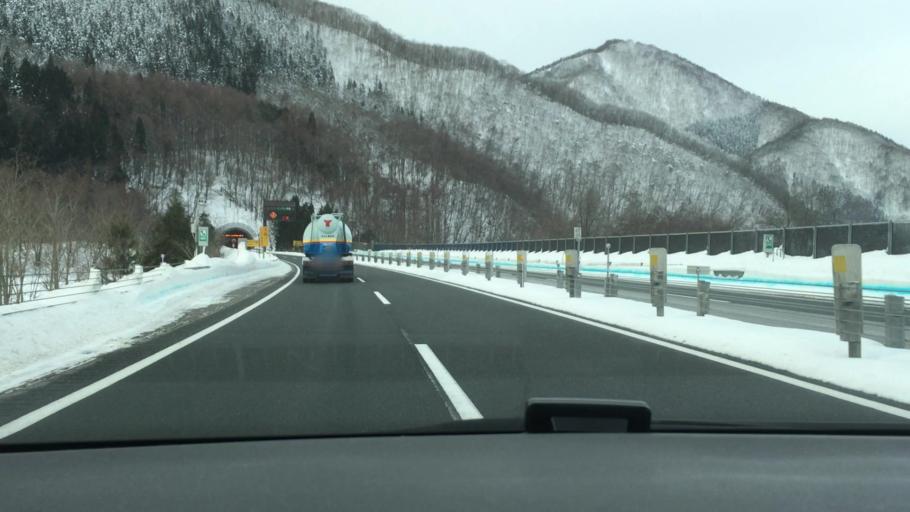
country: JP
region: Akita
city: Hanawa
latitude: 40.1367
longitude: 140.9451
